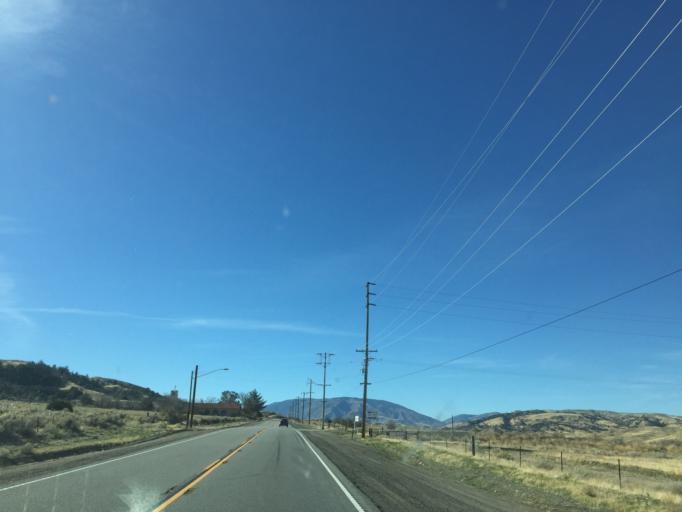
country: US
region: California
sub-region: Kern County
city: Lebec
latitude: 34.7649
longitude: -118.7212
